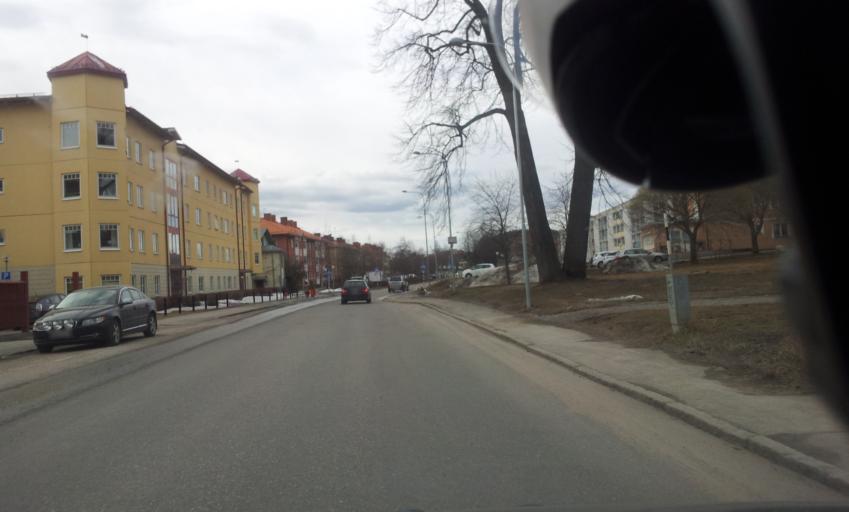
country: SE
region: Gaevleborg
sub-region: Ljusdals Kommun
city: Ljusdal
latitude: 61.8275
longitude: 16.1017
